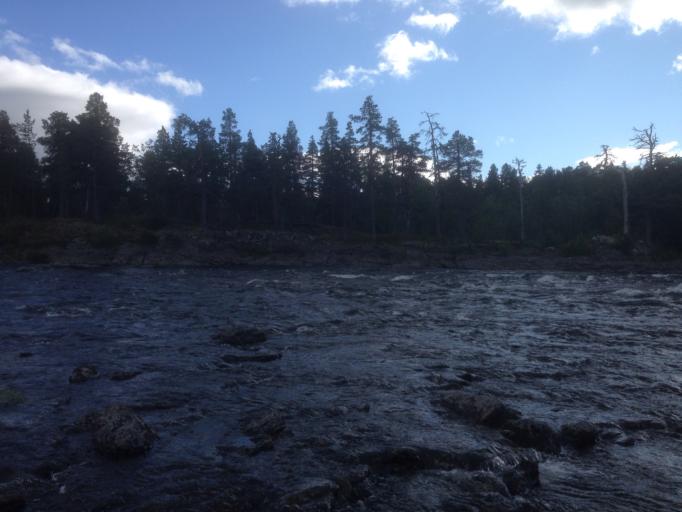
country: SE
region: Norrbotten
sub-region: Arjeplogs Kommun
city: Arjeplog
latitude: 66.4261
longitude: 16.9399
